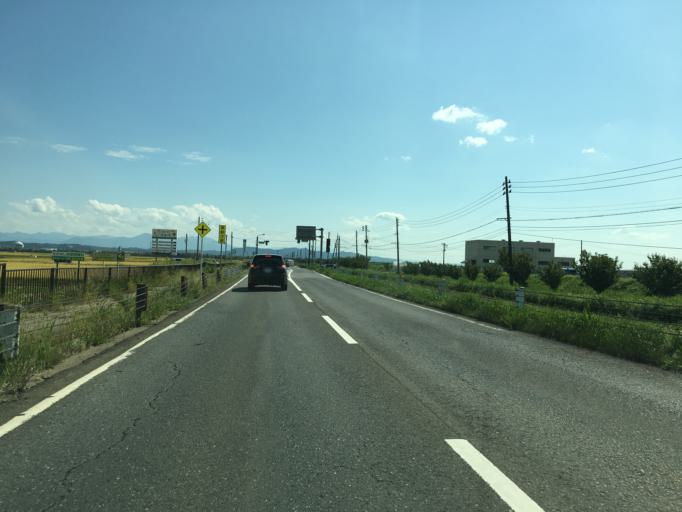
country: JP
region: Niigata
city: Kameda-honcho
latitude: 37.8332
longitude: 139.0967
